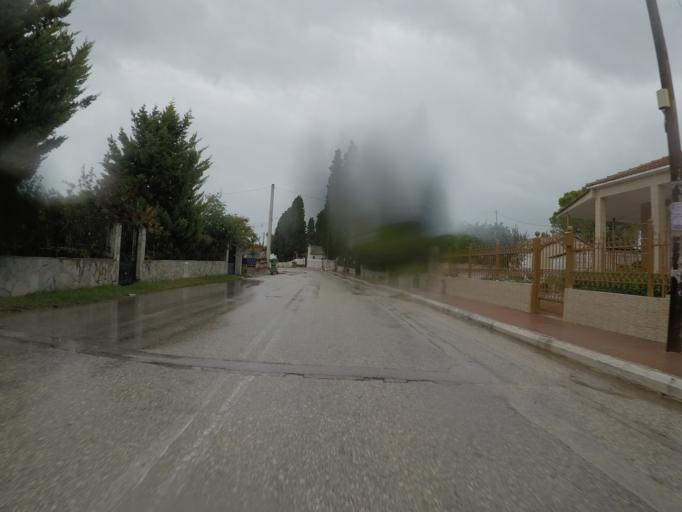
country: GR
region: Peloponnese
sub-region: Nomos Korinthias
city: Arkhaia Korinthos
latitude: 37.9099
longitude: 22.8846
